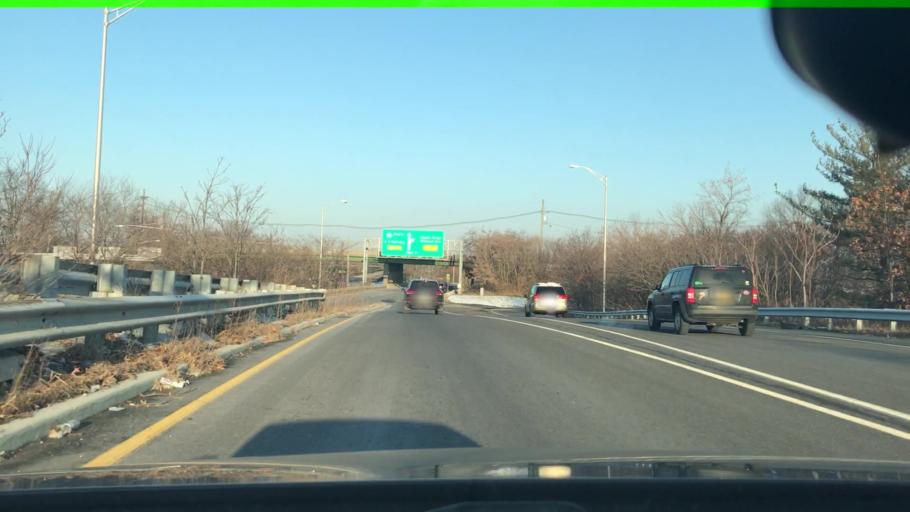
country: US
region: New Jersey
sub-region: Bergen County
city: Saddle Brook
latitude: 40.9049
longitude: -74.0991
